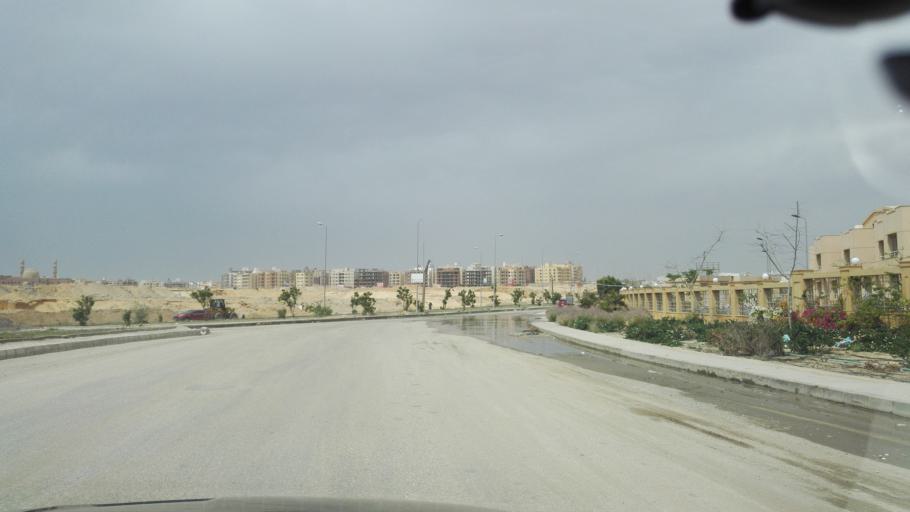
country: EG
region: Muhafazat al Qalyubiyah
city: Al Khankah
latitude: 30.0277
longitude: 31.5296
